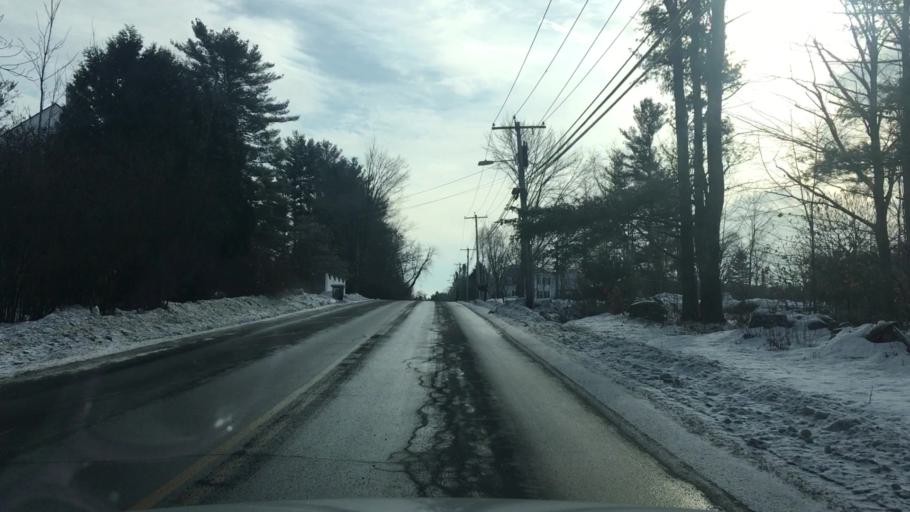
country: US
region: New Hampshire
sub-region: Grafton County
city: Enfield
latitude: 43.6294
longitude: -72.1294
